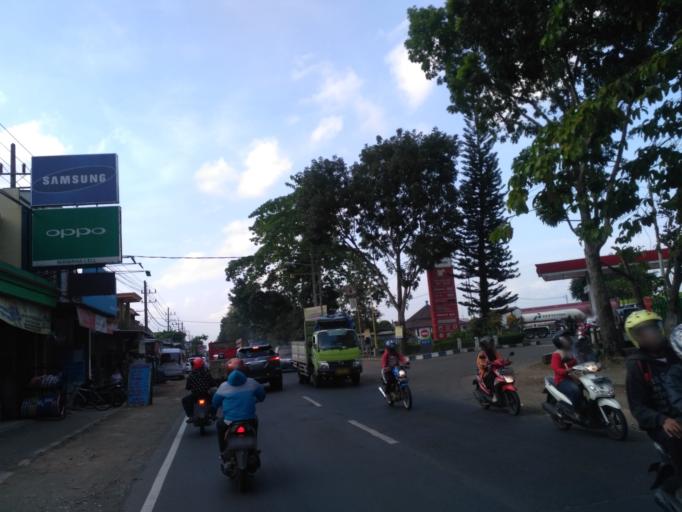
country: ID
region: East Java
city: Pakisaji
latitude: -8.0623
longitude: 112.6007
